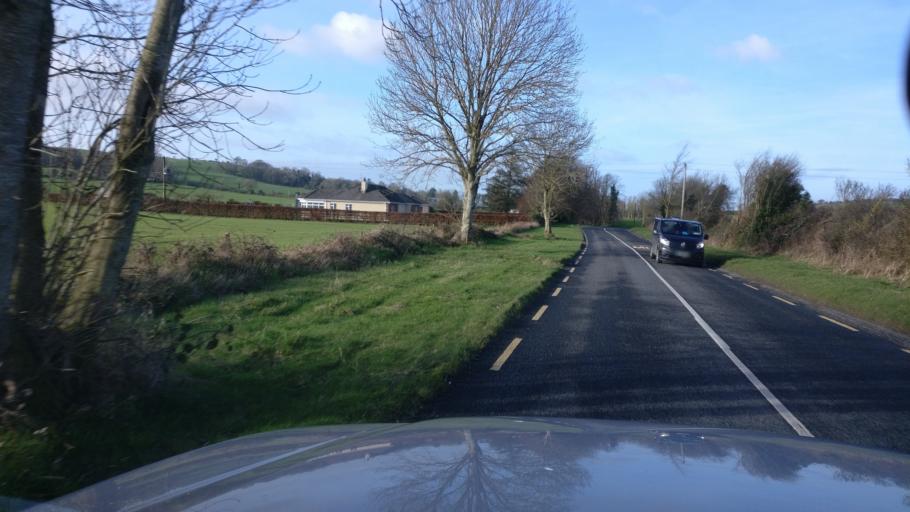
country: IE
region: Leinster
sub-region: Laois
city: Stradbally
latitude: 53.0022
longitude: -7.2250
